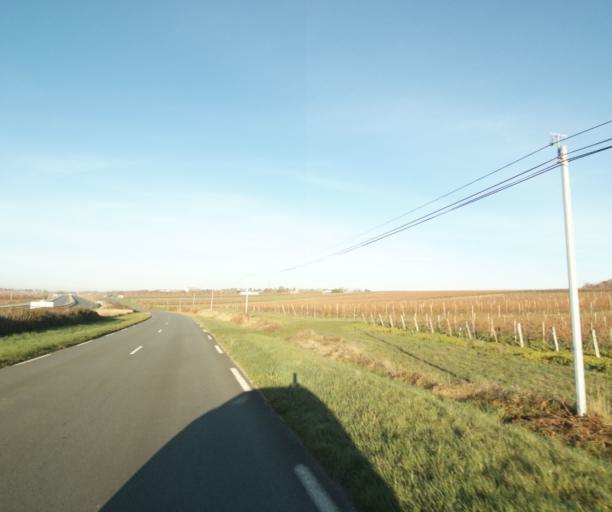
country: FR
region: Poitou-Charentes
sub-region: Departement de la Charente-Maritime
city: Cherac
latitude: 45.6959
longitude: -0.4305
